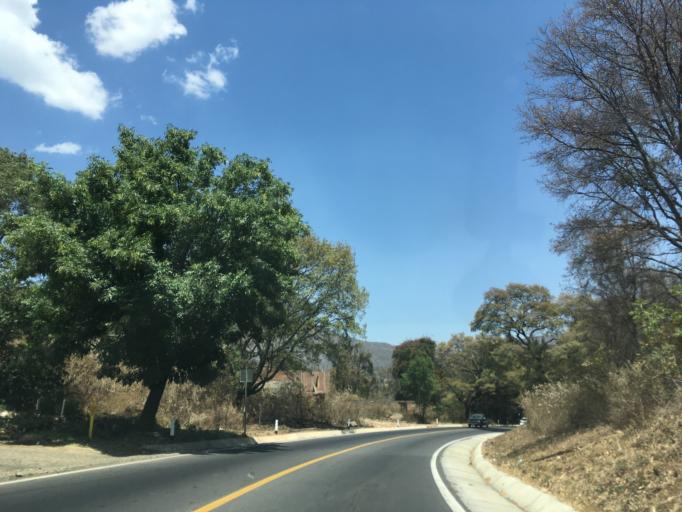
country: MX
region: Michoacan
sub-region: Chilchota
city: Tacuro (Santa Maria Tacuro)
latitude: 19.8482
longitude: -102.0314
